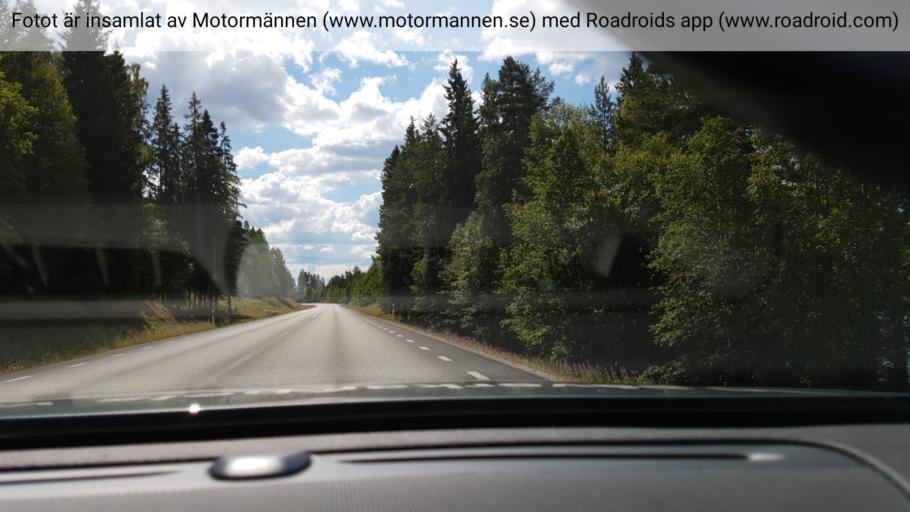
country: SE
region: Dalarna
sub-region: Faluns Kommun
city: Bjursas
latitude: 60.7681
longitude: 15.3179
